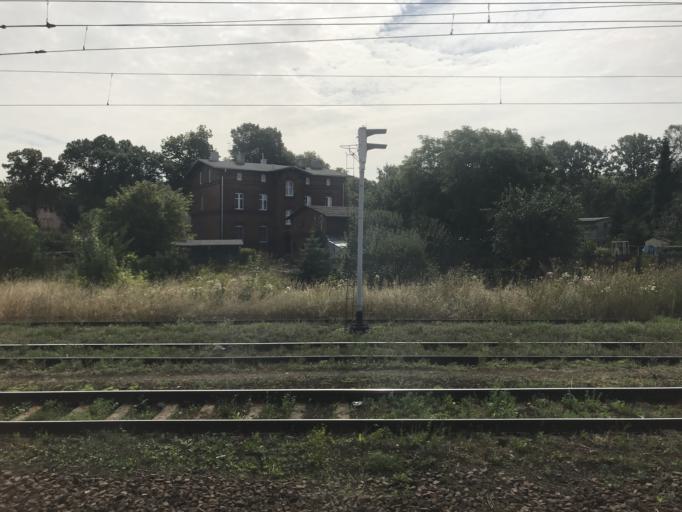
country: PL
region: Kujawsko-Pomorskie
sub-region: Powiat inowroclawski
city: Inowroclaw
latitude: 52.7980
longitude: 18.2365
